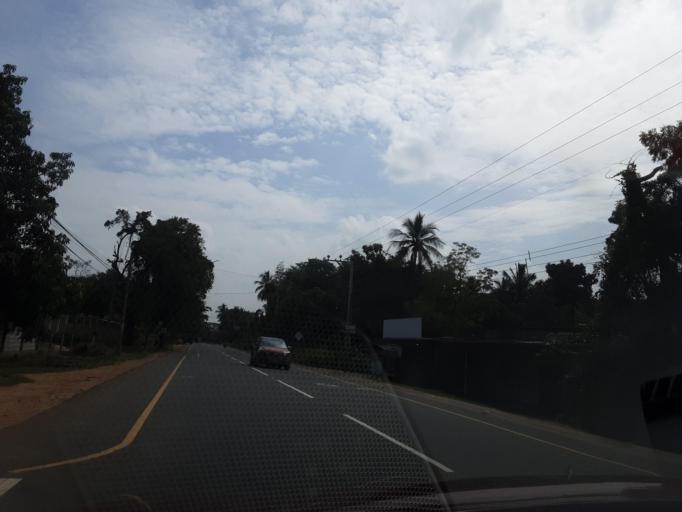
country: LK
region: North Central
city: Anuradhapura
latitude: 8.5226
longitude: 80.5009
